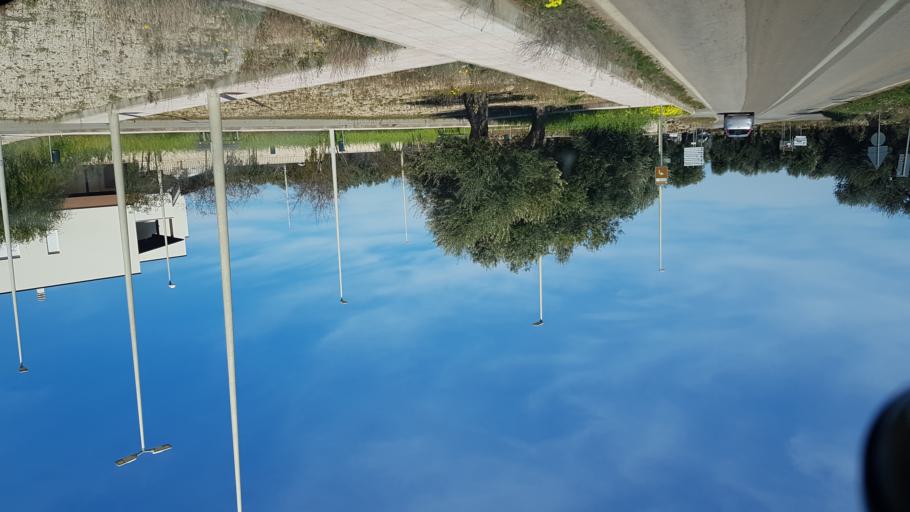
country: IT
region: Apulia
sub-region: Provincia di Brindisi
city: Pezze di Greco
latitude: 40.8356
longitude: 17.4611
